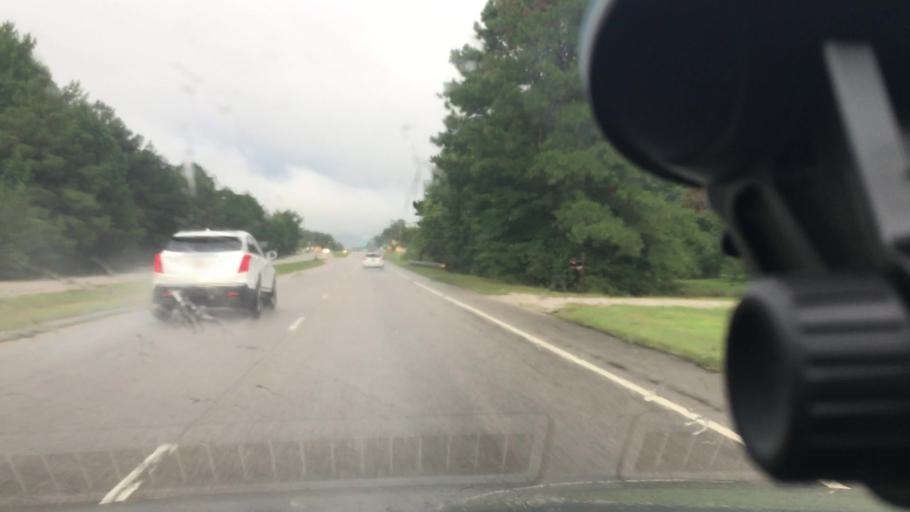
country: US
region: North Carolina
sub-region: Wilson County
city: Wilson
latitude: 35.7644
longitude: -78.0149
